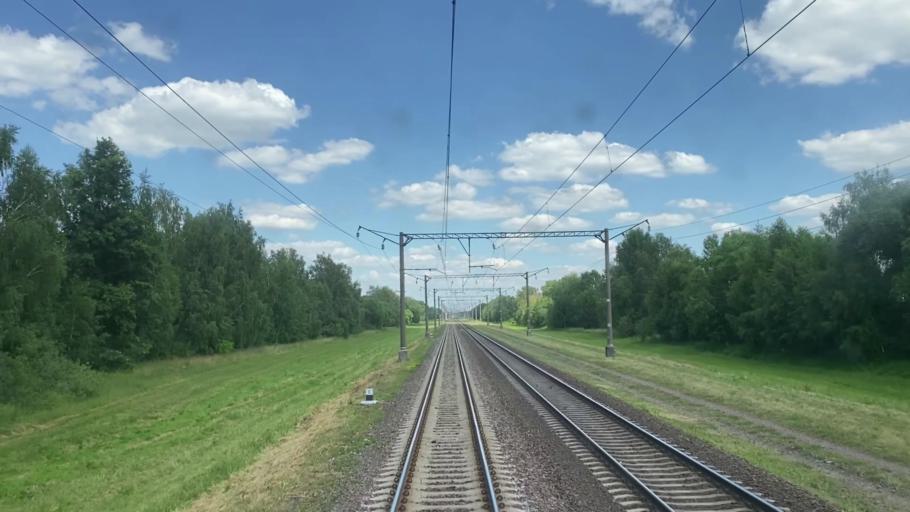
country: BY
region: Brest
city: Charnawchytsy
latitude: 52.1358
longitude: 23.8269
